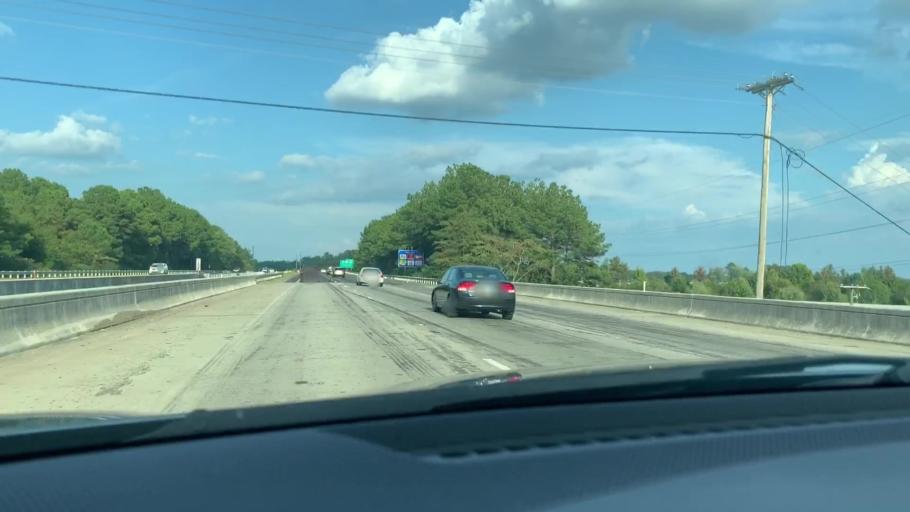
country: US
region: South Carolina
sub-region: Richland County
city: Forest Acres
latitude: 33.9535
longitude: -80.9624
